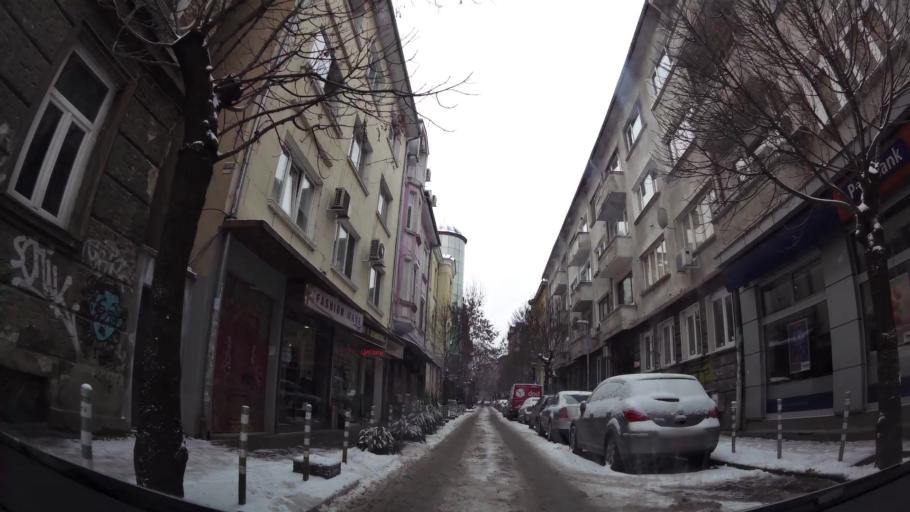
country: BG
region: Sofia-Capital
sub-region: Stolichna Obshtina
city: Sofia
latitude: 42.6924
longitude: 23.3211
